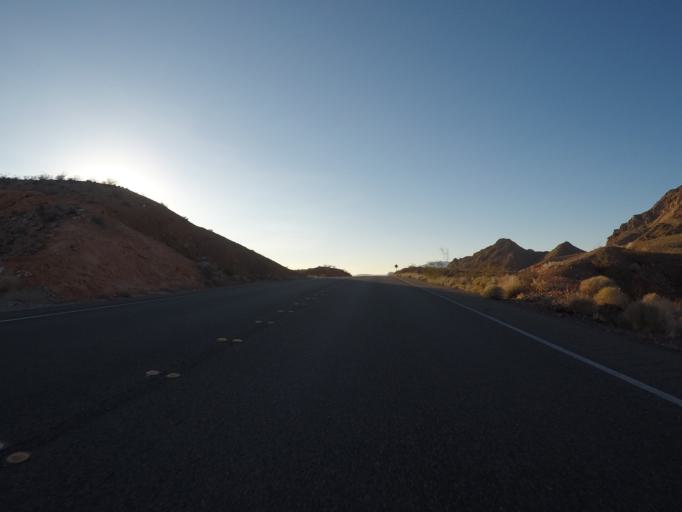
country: US
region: Nevada
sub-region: Clark County
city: Moapa Valley
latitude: 36.2442
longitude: -114.5071
